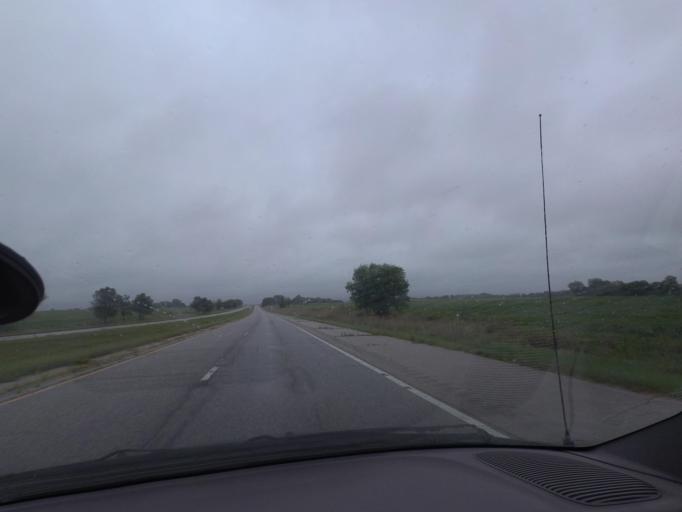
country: US
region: Illinois
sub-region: Pike County
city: Pittsfield
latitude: 39.6699
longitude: -90.8187
